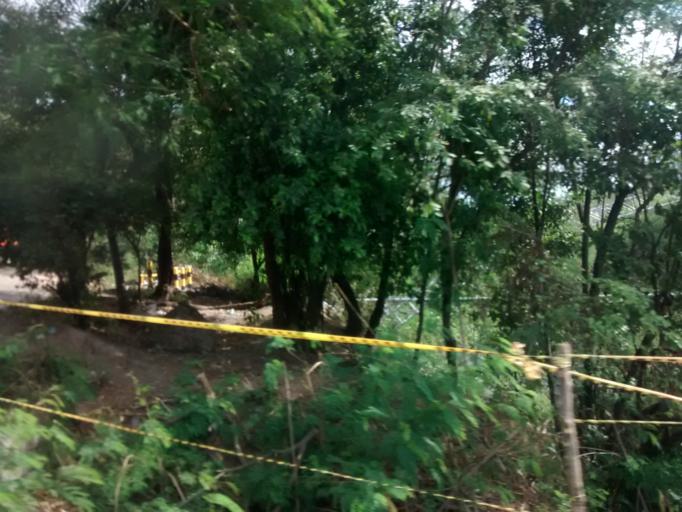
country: CO
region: Cundinamarca
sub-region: Girardot
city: Girardot City
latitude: 4.3014
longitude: -74.7946
